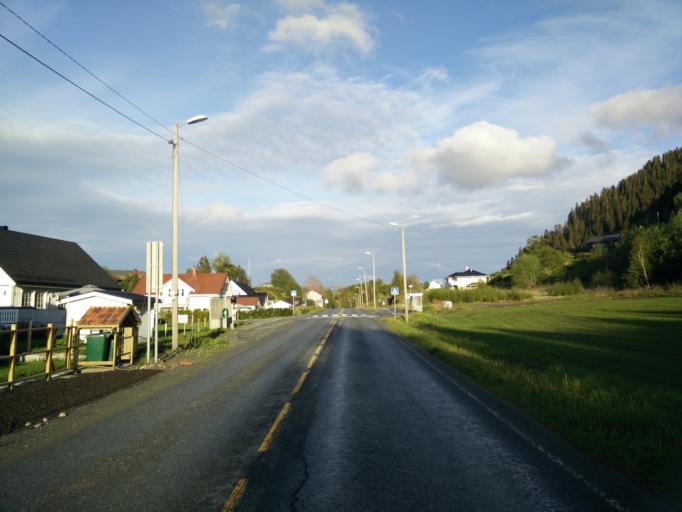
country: NO
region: Sor-Trondelag
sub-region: Skaun
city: Borsa
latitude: 63.3206
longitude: 10.1393
